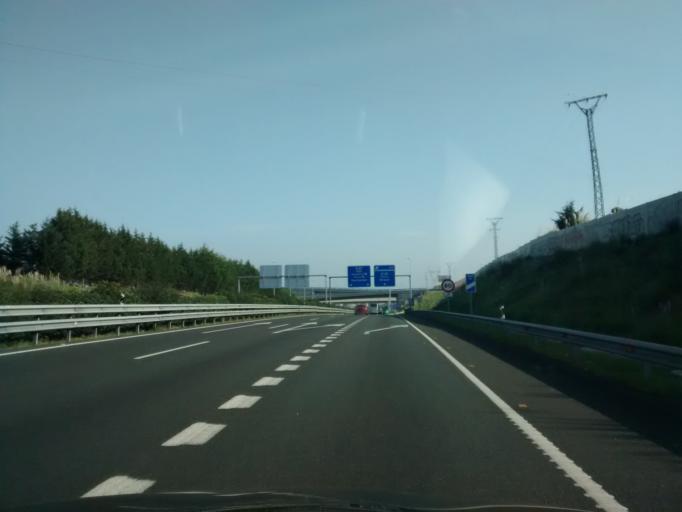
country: ES
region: Cantabria
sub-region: Provincia de Cantabria
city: Santa Cruz de Bezana
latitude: 43.4375
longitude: -3.8808
